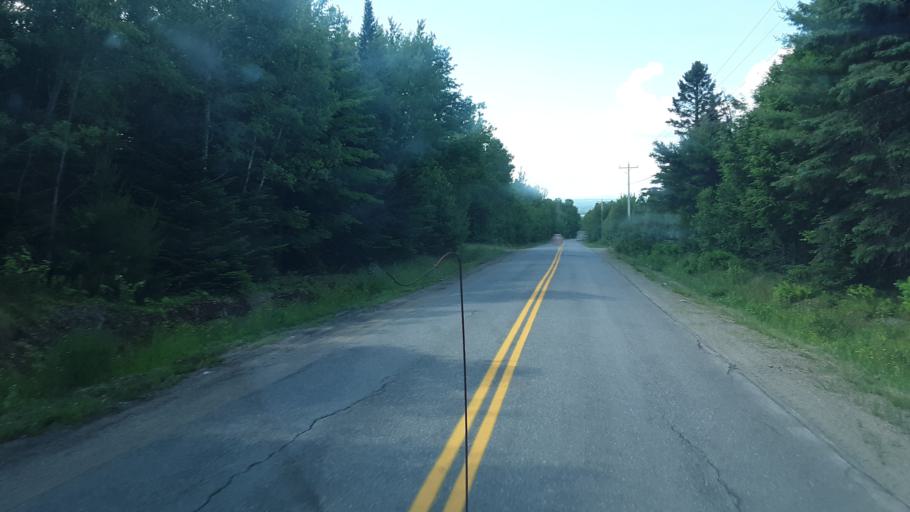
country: US
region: Maine
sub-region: Washington County
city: Calais
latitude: 45.0985
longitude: -67.5096
